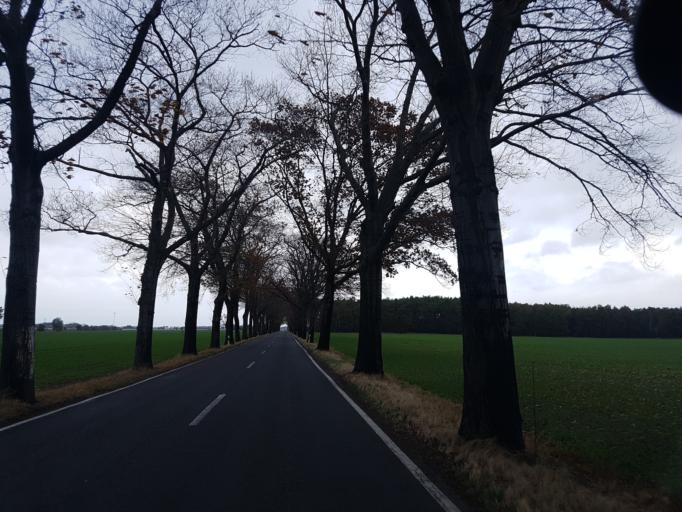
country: DE
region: Brandenburg
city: Herzberg
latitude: 51.6625
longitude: 13.2333
